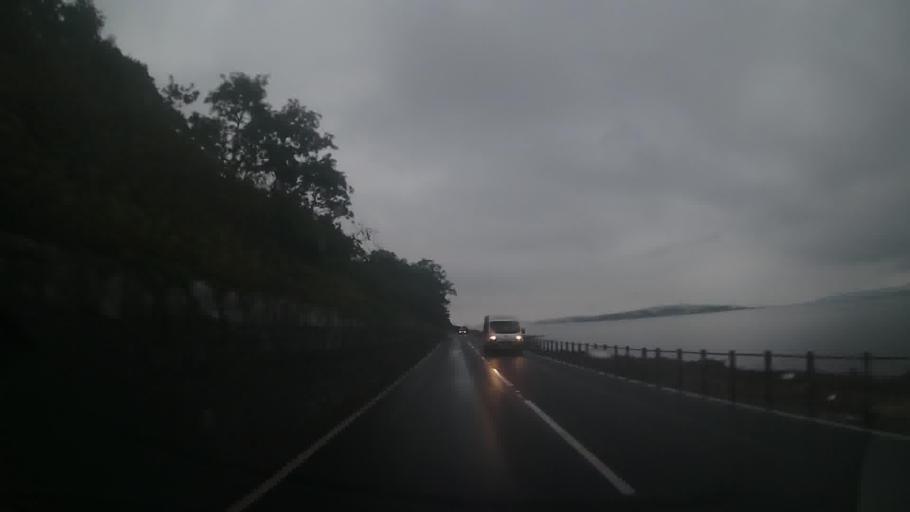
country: GB
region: Scotland
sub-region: North Ayrshire
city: Largs
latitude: 55.8230
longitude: -4.8885
